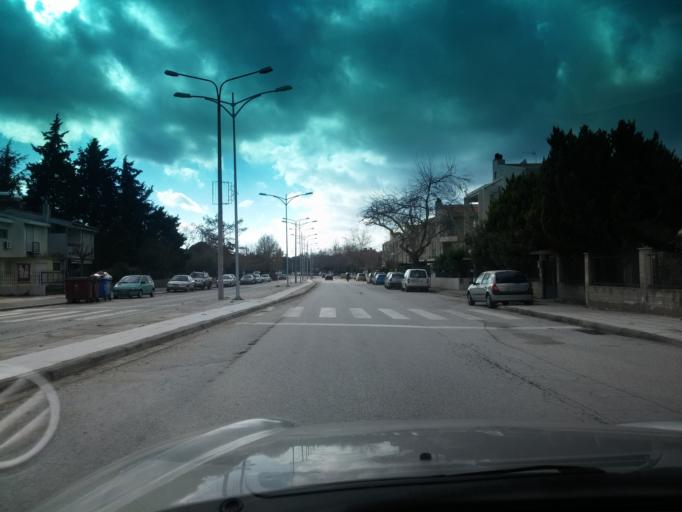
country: GR
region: East Macedonia and Thrace
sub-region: Nomos Rodopis
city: Komotini
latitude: 41.1237
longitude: 25.3907
